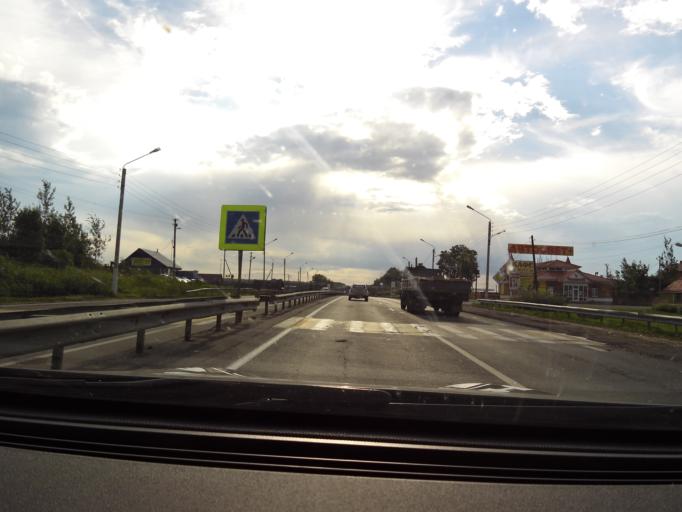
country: RU
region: Vladimir
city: Novovyazniki
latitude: 56.2031
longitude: 42.3150
